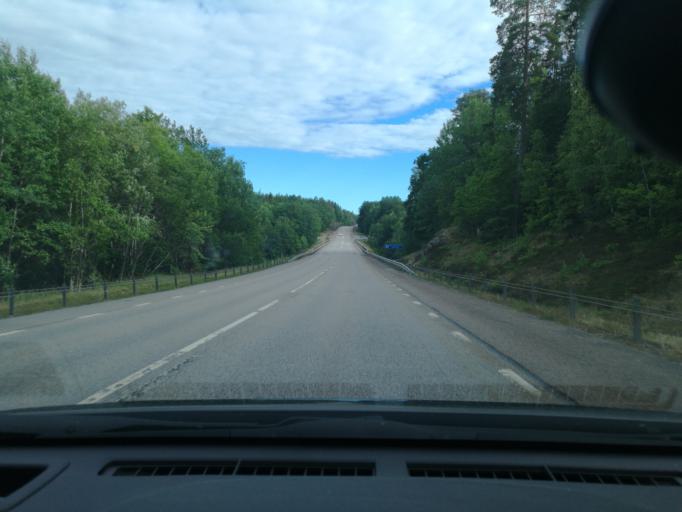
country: SE
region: Kalmar
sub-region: Vasterviks Kommun
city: Ankarsrum
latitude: 57.5518
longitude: 16.4758
